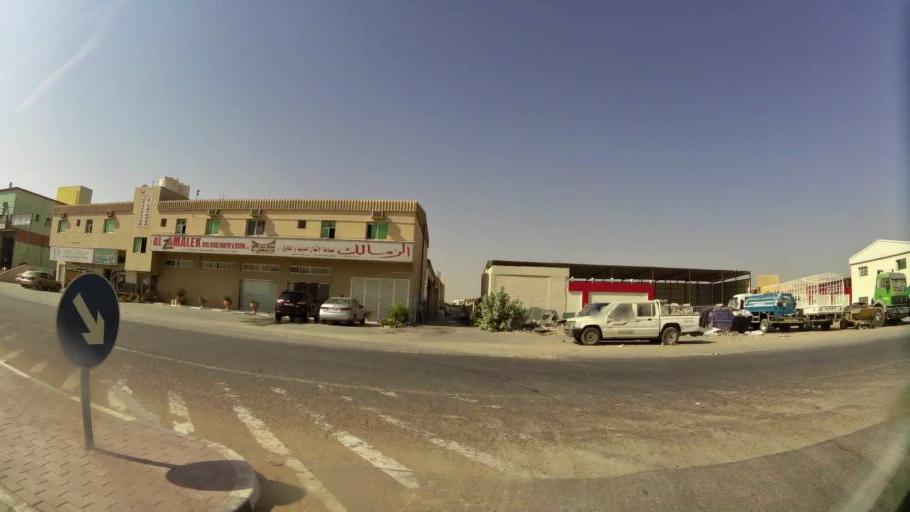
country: AE
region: Ajman
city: Ajman
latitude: 25.4387
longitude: 55.5260
